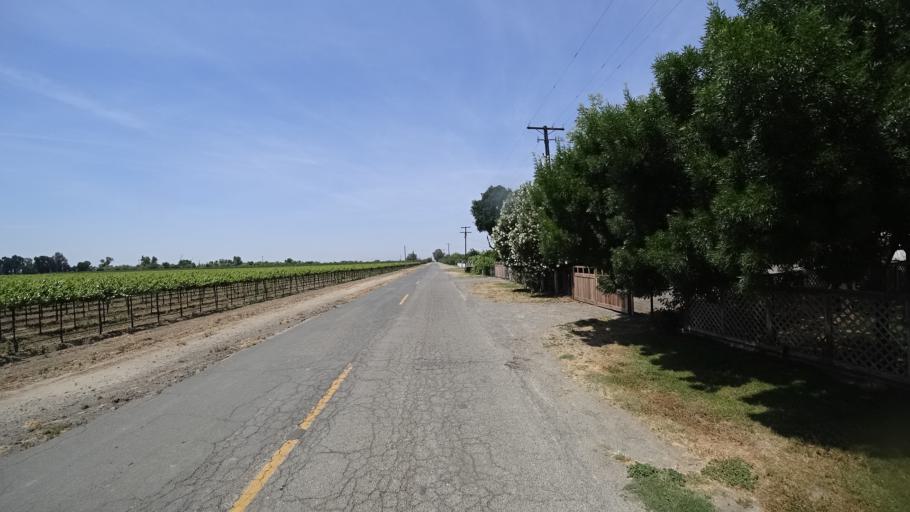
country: US
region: California
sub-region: Fresno County
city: Riverdale
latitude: 36.3875
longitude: -119.8614
